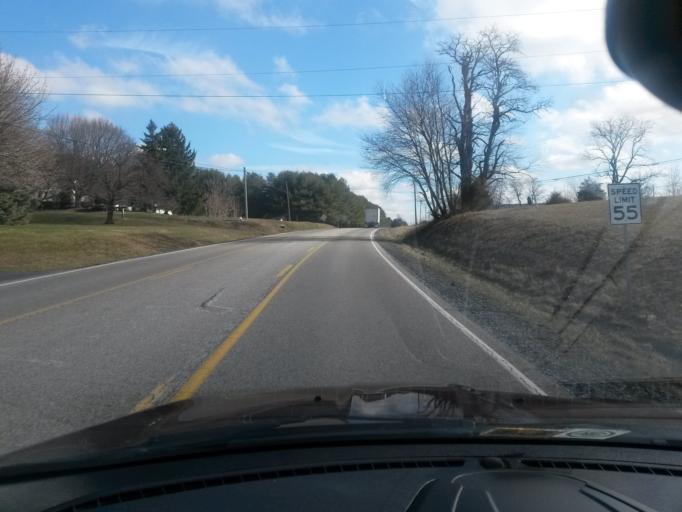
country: US
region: Virginia
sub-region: Augusta County
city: Jolivue
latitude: 38.0344
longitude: -79.1368
